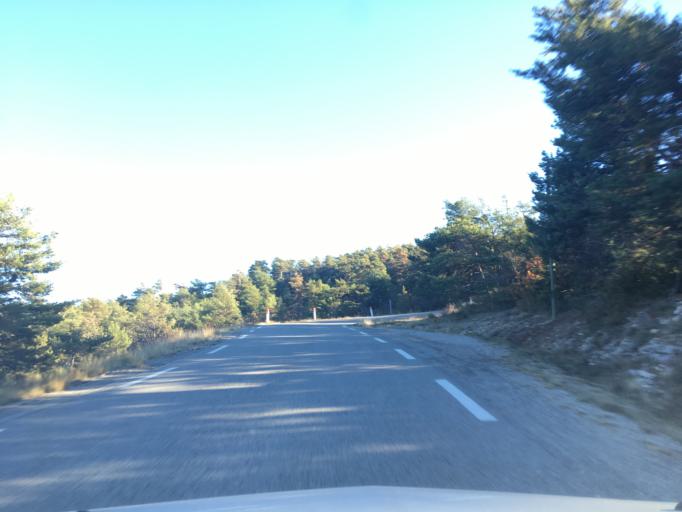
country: FR
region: Provence-Alpes-Cote d'Azur
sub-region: Departement des Alpes-de-Haute-Provence
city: Castellane
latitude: 43.7472
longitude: 6.4354
